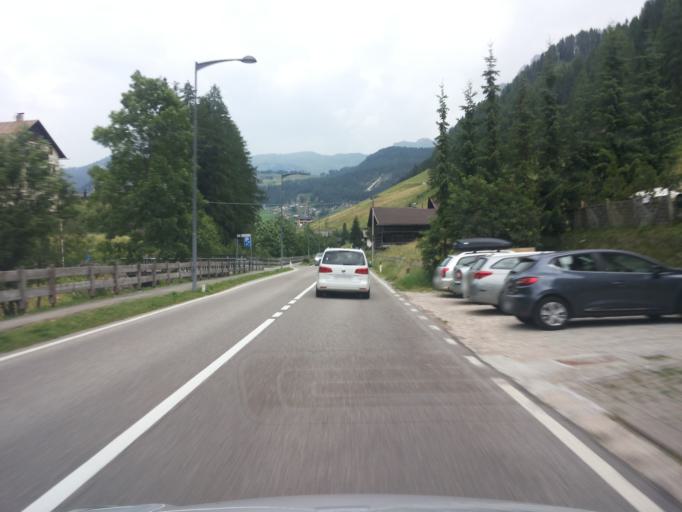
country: IT
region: Trentino-Alto Adige
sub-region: Bolzano
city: Selva
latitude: 46.5470
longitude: 11.7680
